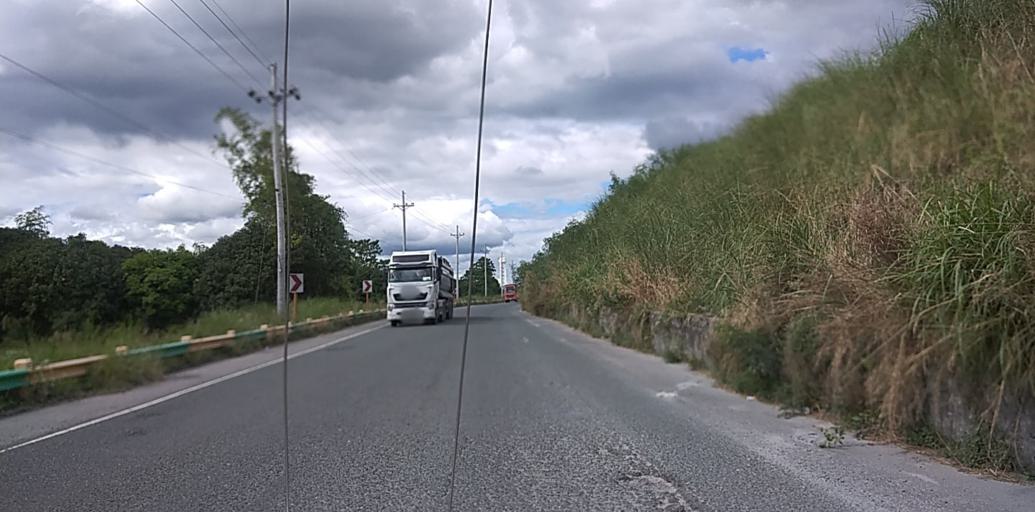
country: PH
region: Central Luzon
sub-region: Province of Pampanga
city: Dolores
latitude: 15.1054
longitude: 120.5211
